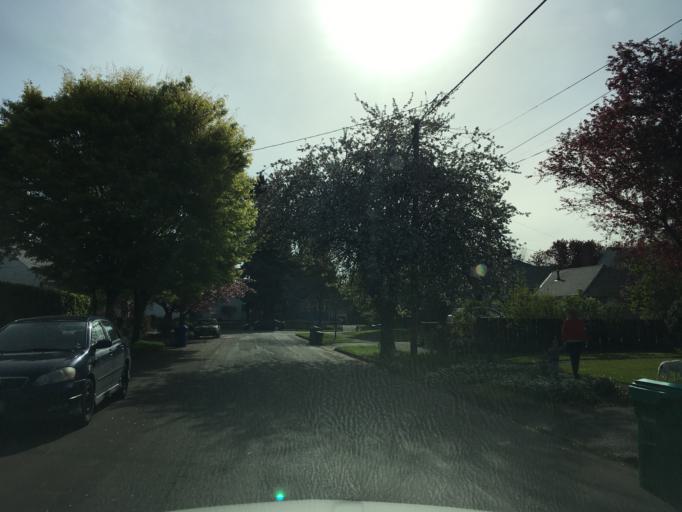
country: US
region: Oregon
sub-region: Multnomah County
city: Lents
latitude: 45.5211
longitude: -122.5748
